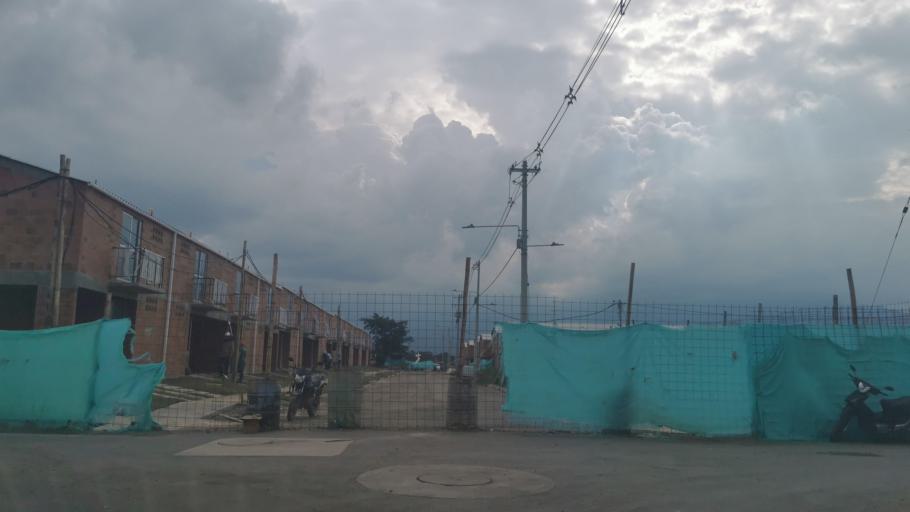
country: CO
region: Valle del Cauca
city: Jamundi
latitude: 3.2333
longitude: -76.5261
